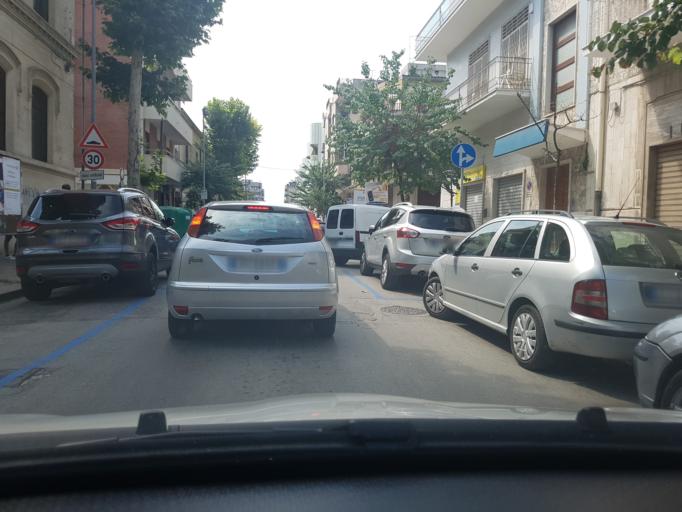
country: IT
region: Apulia
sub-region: Provincia di Foggia
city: Cerignola
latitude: 41.2652
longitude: 15.9033
